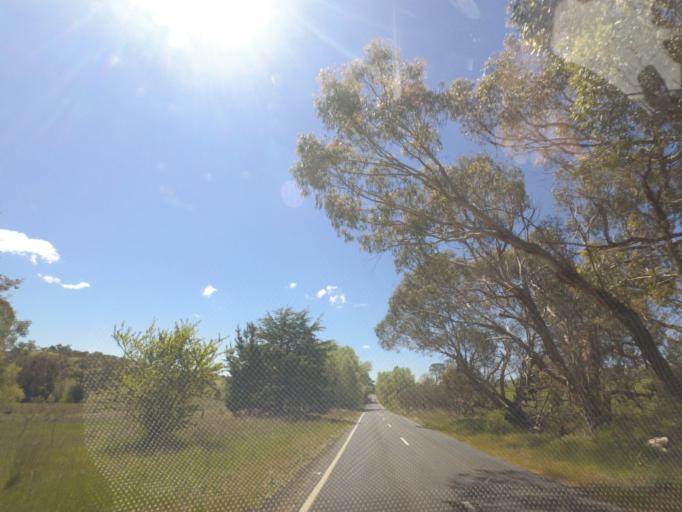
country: AU
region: Victoria
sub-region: Hume
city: Sunbury
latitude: -37.1068
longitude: 144.7593
